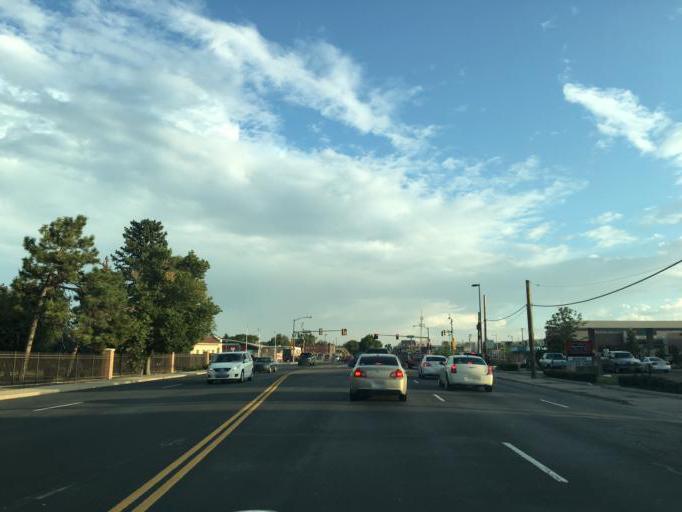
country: US
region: Colorado
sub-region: Adams County
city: Aurora
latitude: 39.7414
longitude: -104.8471
